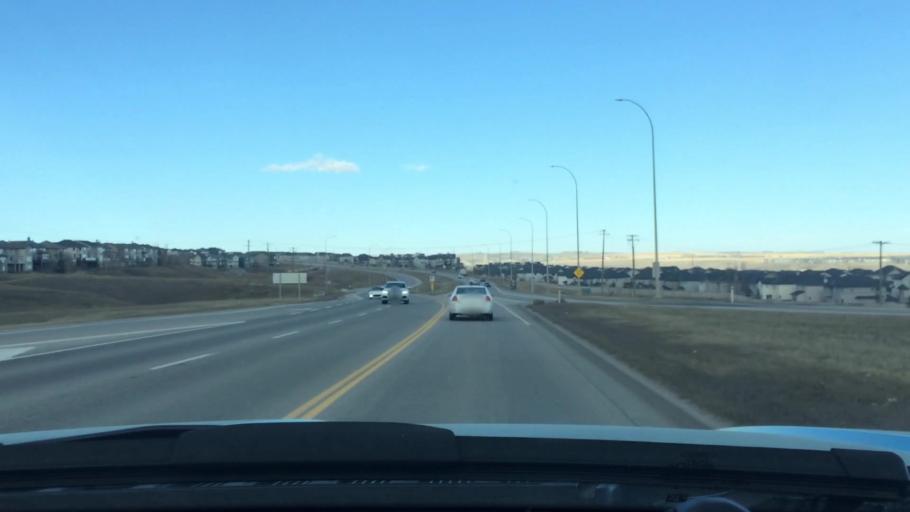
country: CA
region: Alberta
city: Calgary
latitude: 51.1559
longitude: -114.1410
